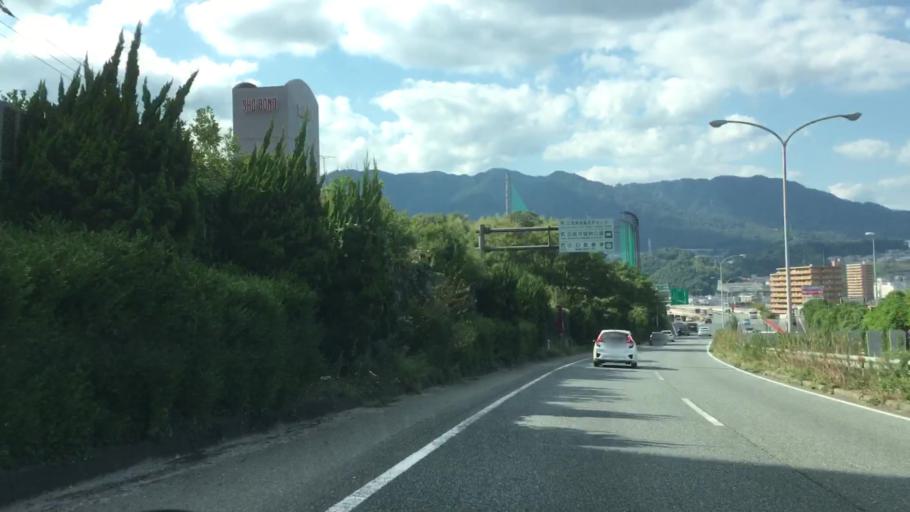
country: JP
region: Hiroshima
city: Hatsukaichi
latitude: 34.3770
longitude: 132.3673
